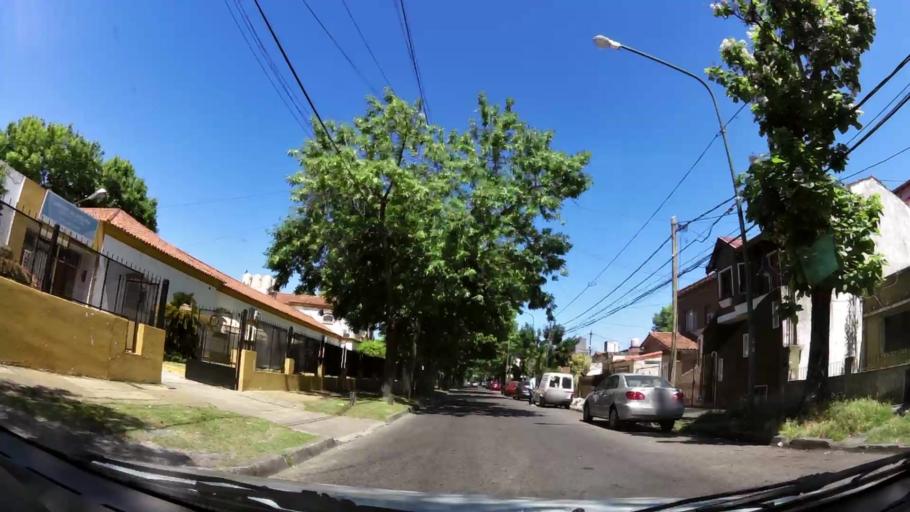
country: AR
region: Buenos Aires
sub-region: Partido de Vicente Lopez
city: Olivos
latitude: -34.5136
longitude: -58.5038
